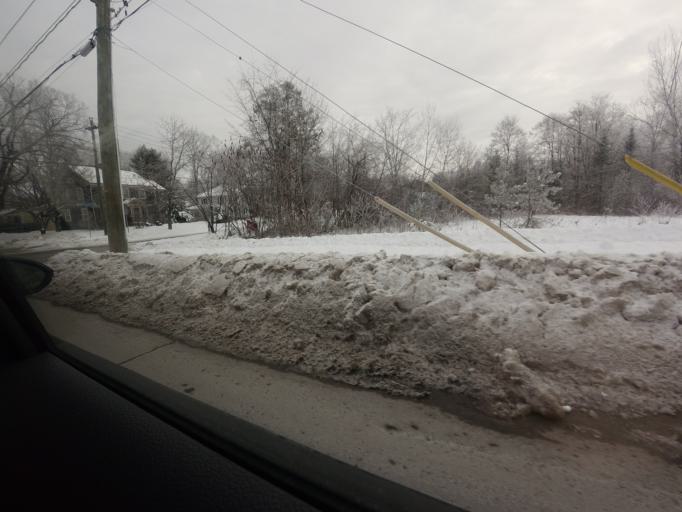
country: CA
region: New Brunswick
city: Fredericton
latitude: 45.9497
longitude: -66.6390
